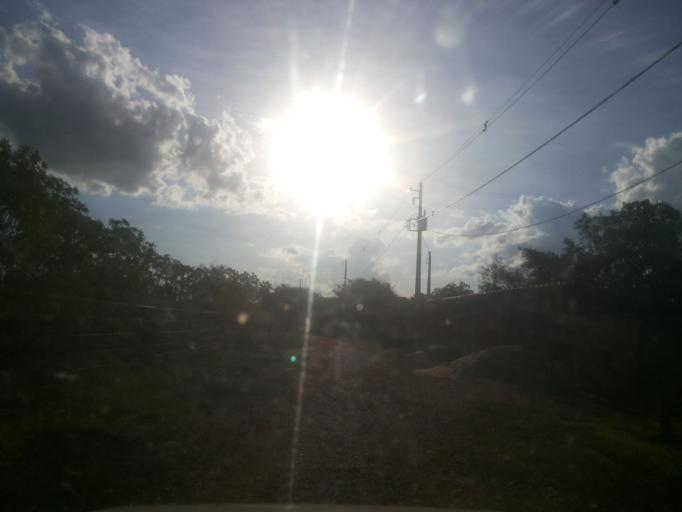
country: BR
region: Minas Gerais
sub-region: Santa Vitoria
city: Santa Vitoria
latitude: -18.9851
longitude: -50.3641
